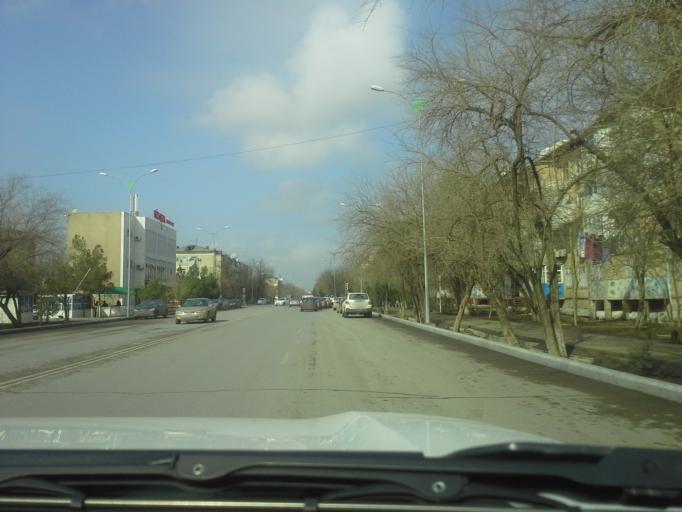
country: TM
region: Mary
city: Mary
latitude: 37.5931
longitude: 61.8302
